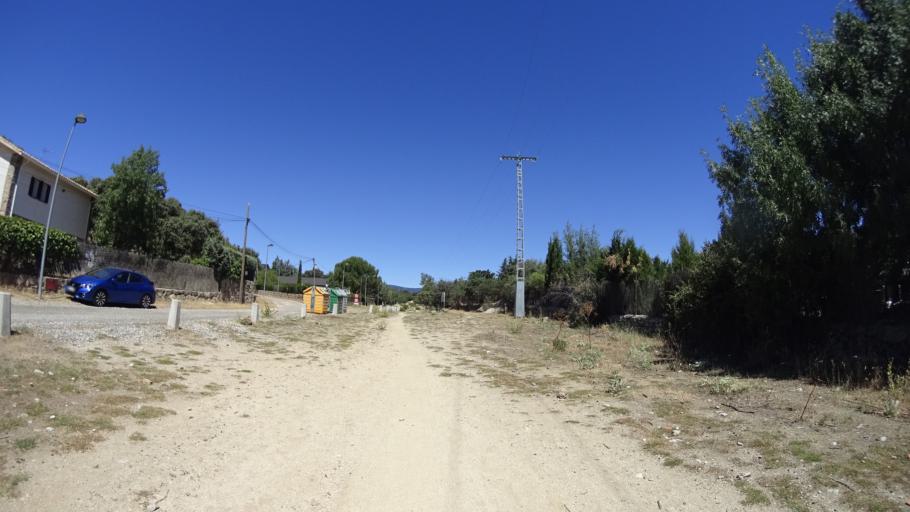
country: ES
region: Madrid
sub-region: Provincia de Madrid
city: Alpedrete
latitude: 40.6522
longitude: -4.0424
